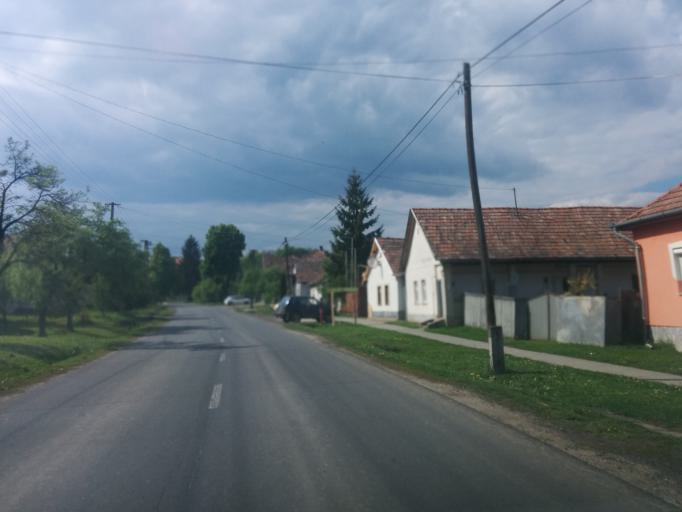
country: HU
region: Nograd
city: Romhany
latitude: 47.8449
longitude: 19.2961
